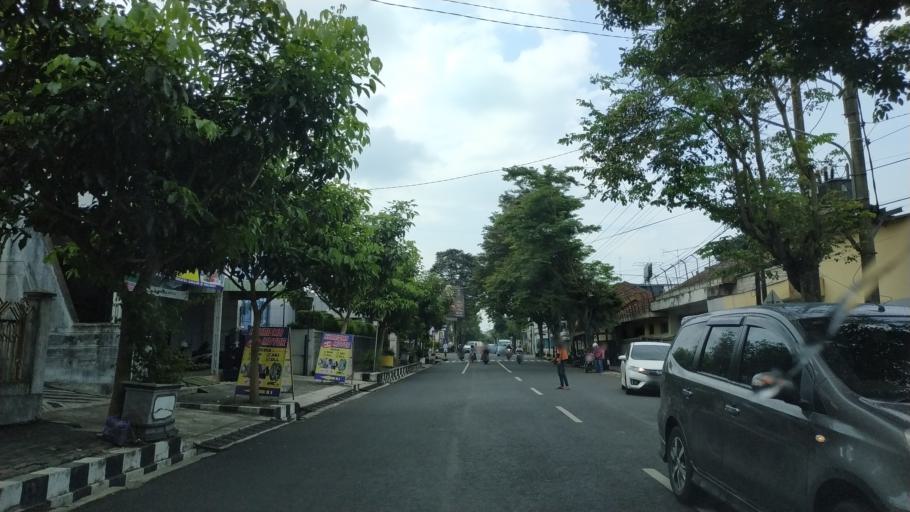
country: ID
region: Central Java
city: Magelang
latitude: -7.3173
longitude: 110.1770
